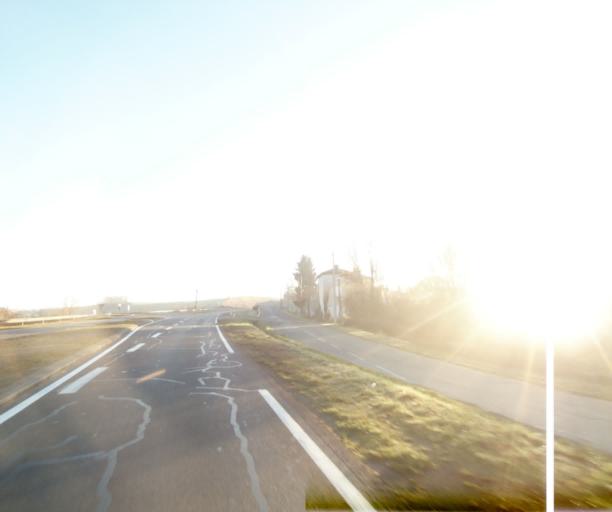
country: FR
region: Poitou-Charentes
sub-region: Departement de la Charente-Maritime
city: Chaniers
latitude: 45.7278
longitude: -0.5139
